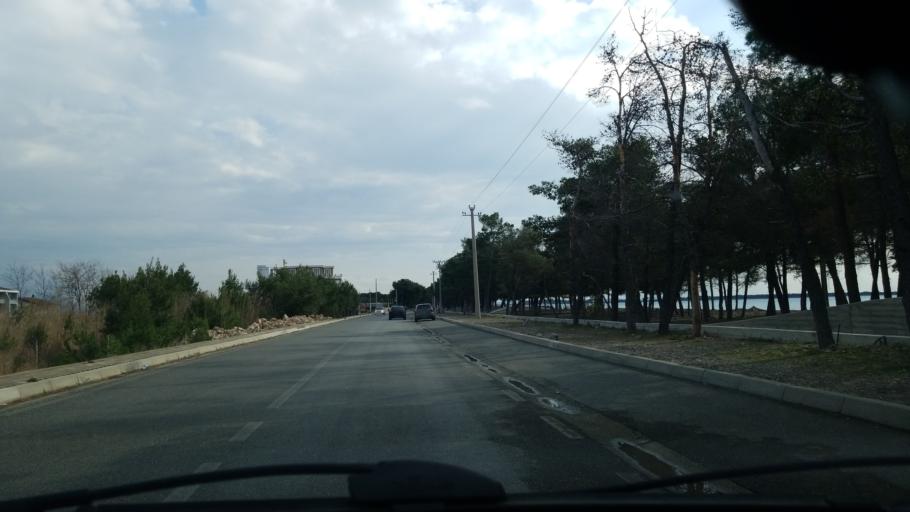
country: AL
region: Lezhe
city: Shengjin
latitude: 41.7916
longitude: 19.6030
